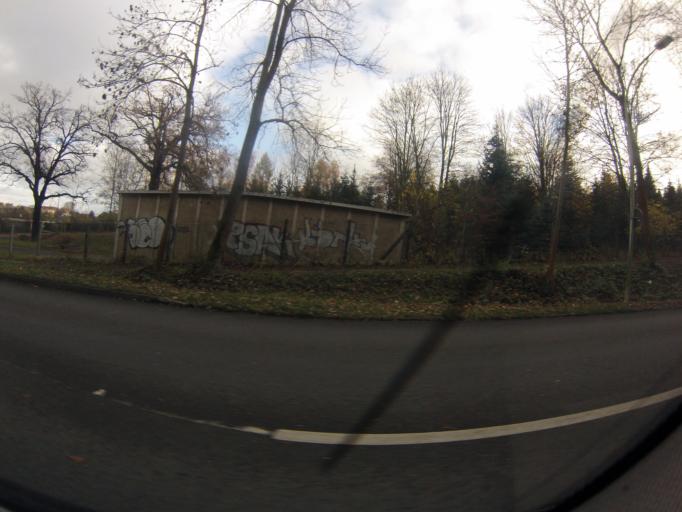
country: DE
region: Thuringia
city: Altenburg
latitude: 50.9740
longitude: 12.4340
